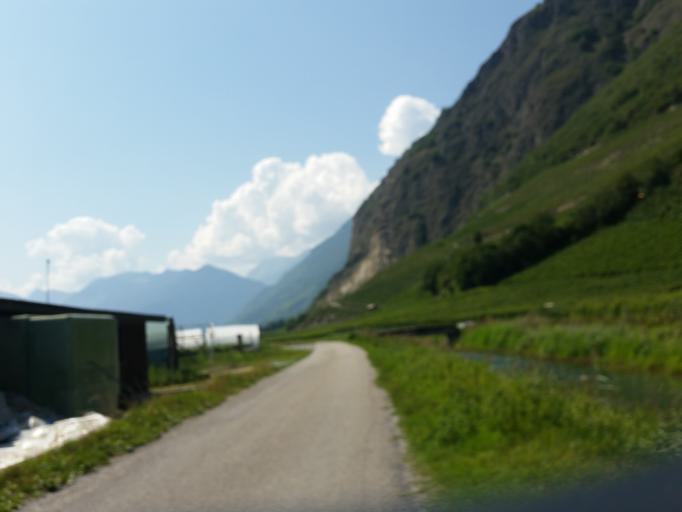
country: CH
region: Valais
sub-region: Martigny District
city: Saxon
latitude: 46.1613
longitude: 7.1635
